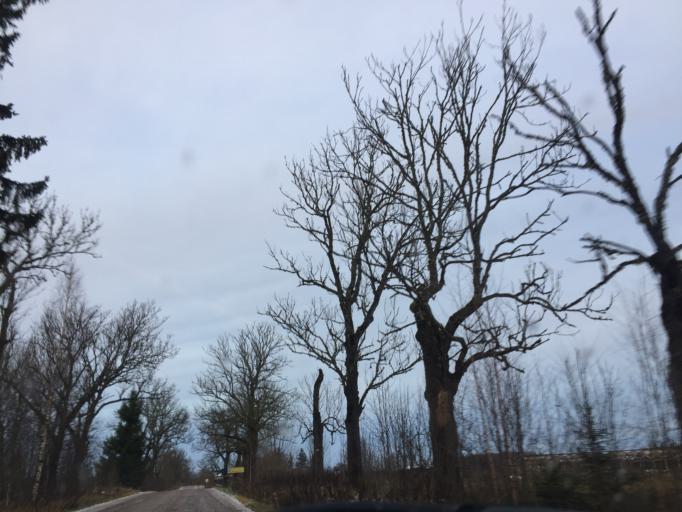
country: LV
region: Limbazu Rajons
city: Limbazi
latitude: 57.5484
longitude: 24.8122
